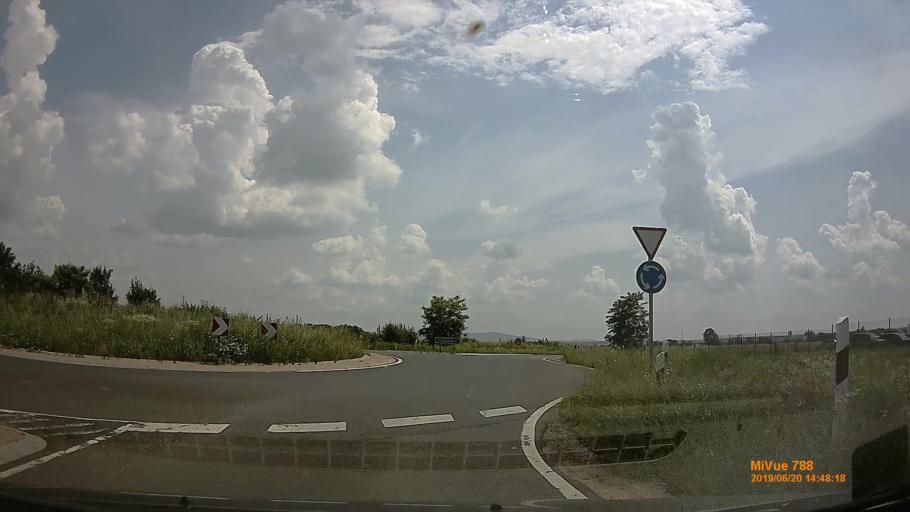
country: HU
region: Baranya
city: Kozarmisleny
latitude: 46.0156
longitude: 18.2887
